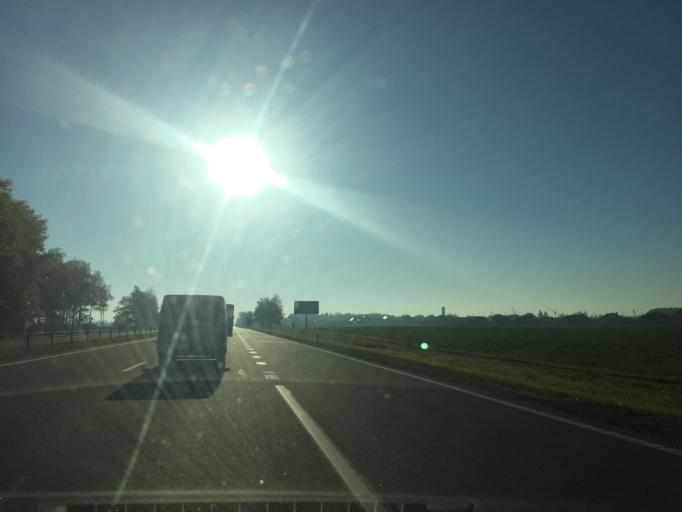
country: BY
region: Minsk
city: Luhavaya Slabada
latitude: 53.7896
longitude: 27.8247
